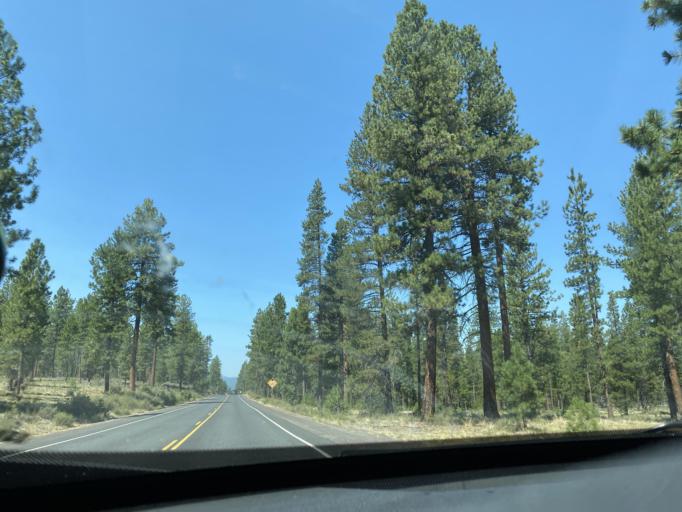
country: US
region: Oregon
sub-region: Deschutes County
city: Sunriver
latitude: 43.8914
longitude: -121.4056
